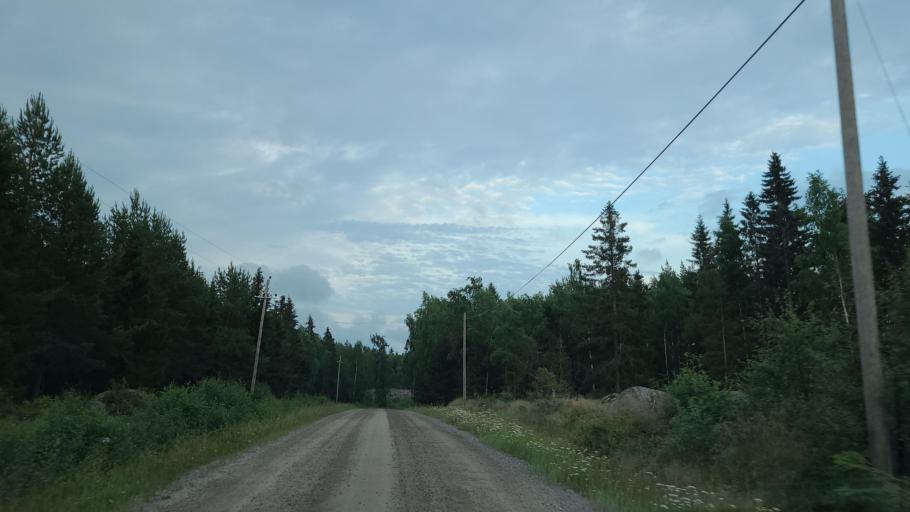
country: FI
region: Ostrobothnia
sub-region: Vaasa
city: Replot
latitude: 63.3165
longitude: 21.1551
